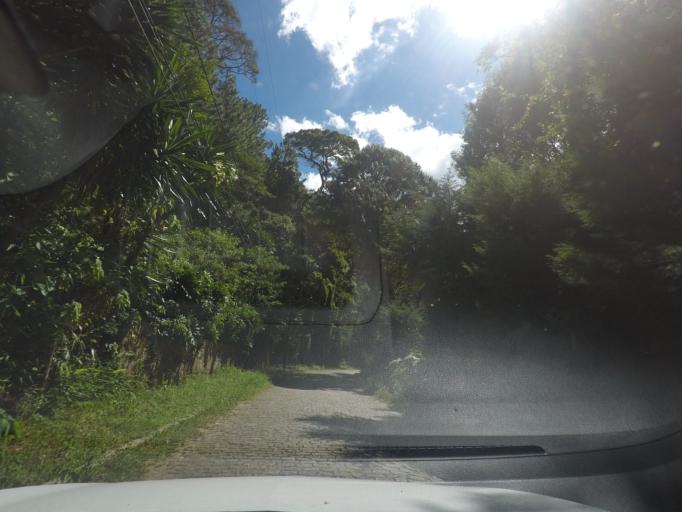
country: BR
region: Rio de Janeiro
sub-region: Teresopolis
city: Teresopolis
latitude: -22.4331
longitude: -42.9917
